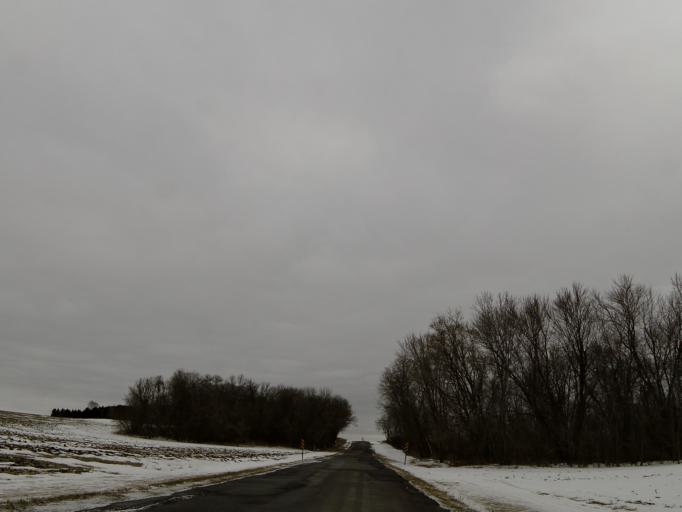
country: US
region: Minnesota
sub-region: Dakota County
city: Hastings
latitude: 44.8039
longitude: -92.8736
